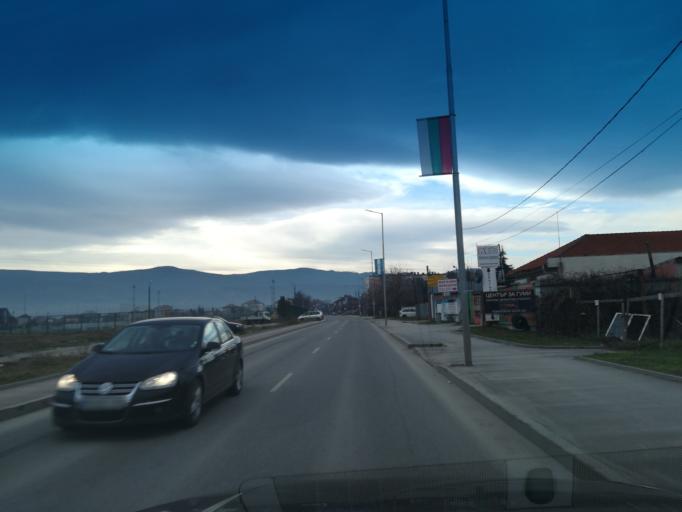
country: BG
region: Plovdiv
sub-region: Obshtina Plovdiv
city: Plovdiv
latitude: 42.1101
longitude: 24.7078
